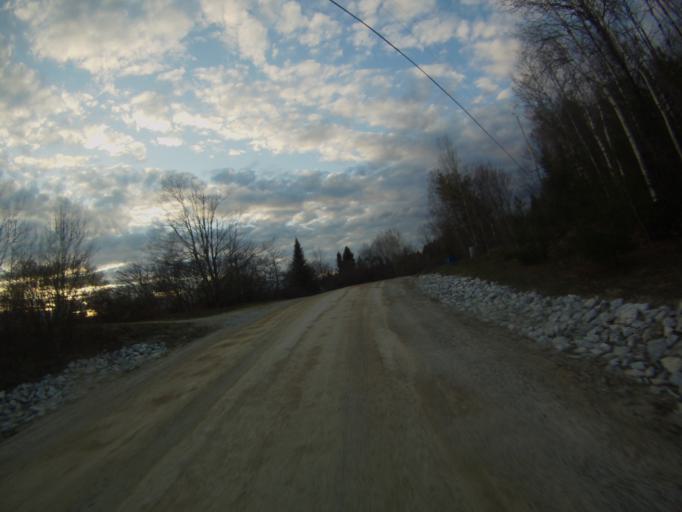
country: US
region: Vermont
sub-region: Rutland County
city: Brandon
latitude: 43.8999
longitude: -73.0150
